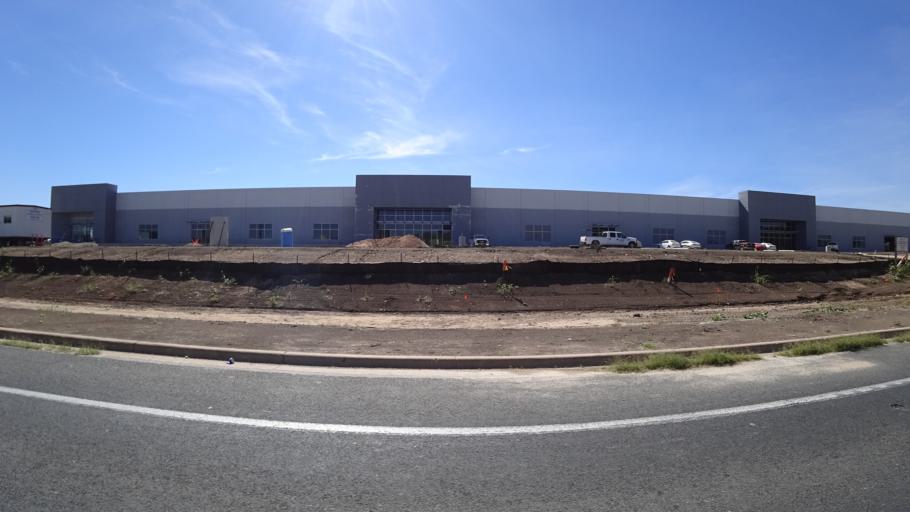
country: US
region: Texas
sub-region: Travis County
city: Austin
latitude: 30.1841
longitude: -97.6895
